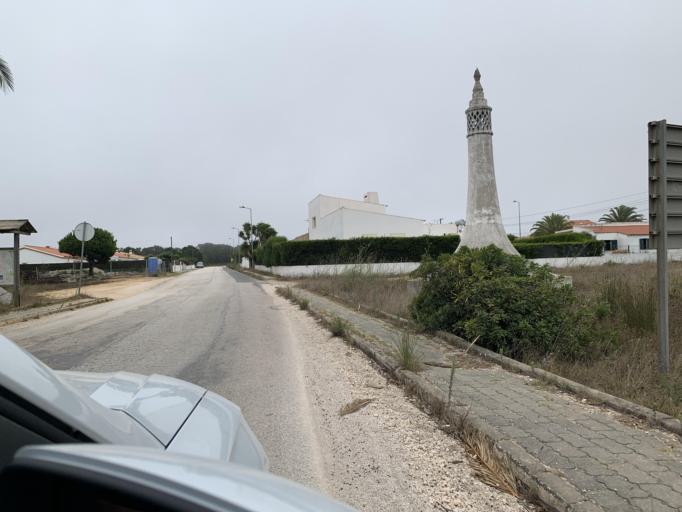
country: PT
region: Faro
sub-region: Aljezur
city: Aljezur
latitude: 37.3025
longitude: -8.8488
